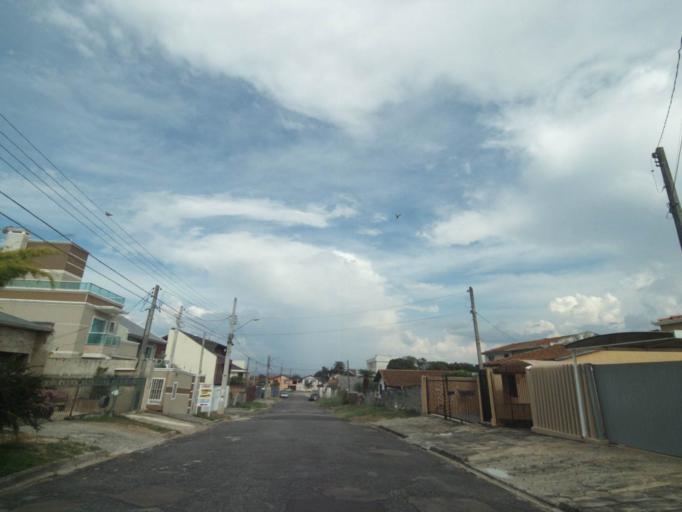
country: BR
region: Parana
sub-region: Pinhais
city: Pinhais
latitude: -25.4431
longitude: -49.2239
